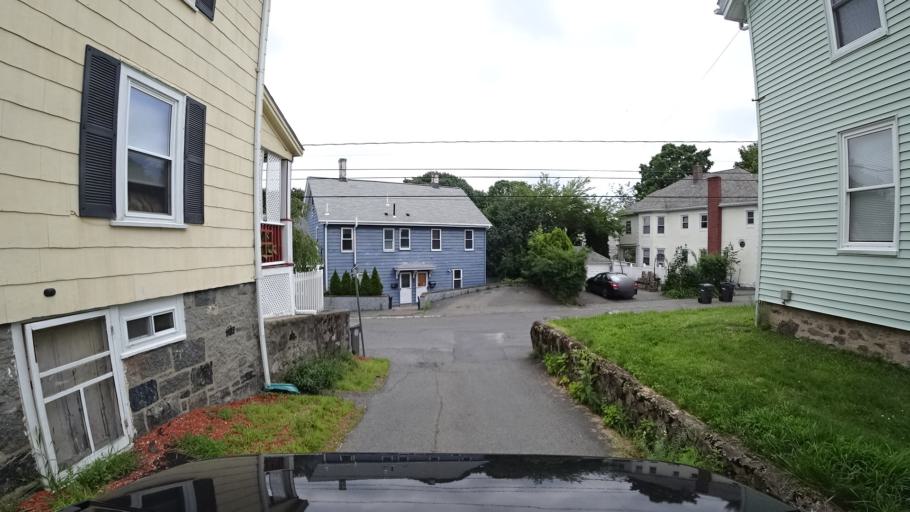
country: US
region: Massachusetts
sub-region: Norfolk County
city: Dedham
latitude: 42.2527
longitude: -71.1559
